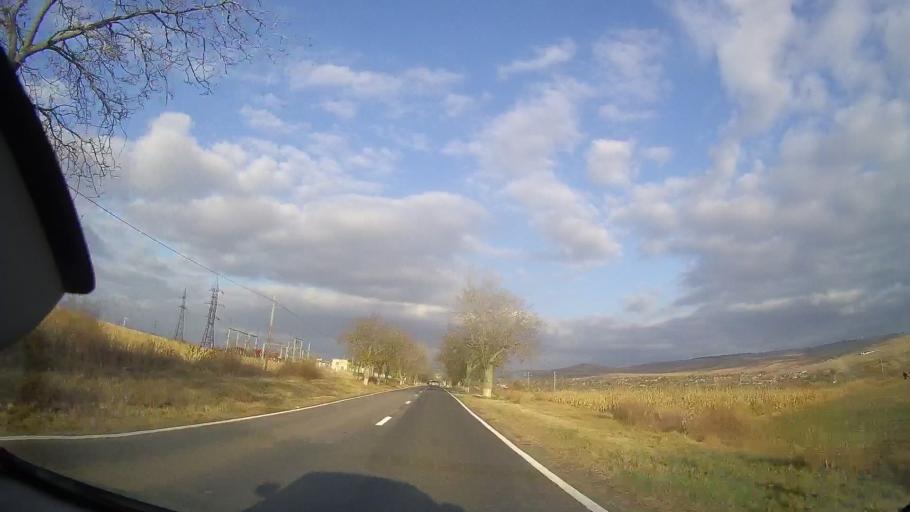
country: RO
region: Tulcea
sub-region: Comuna Topolog
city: Topolog
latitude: 44.8684
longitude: 28.3617
